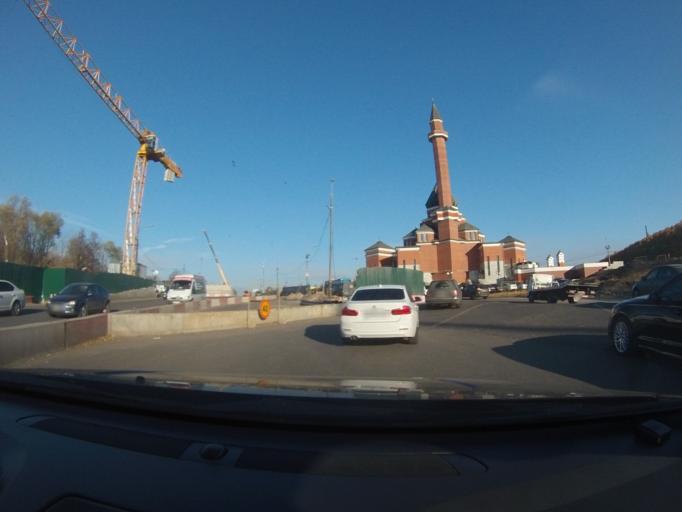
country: RU
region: Moskovskaya
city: Kastanayevo
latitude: 55.7246
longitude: 37.4970
